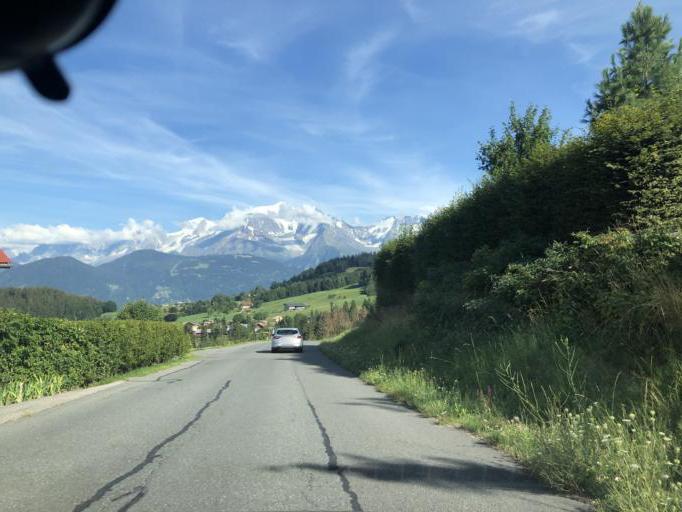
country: FR
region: Rhone-Alpes
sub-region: Departement de la Haute-Savoie
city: Cordon
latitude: 45.9153
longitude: 6.6036
